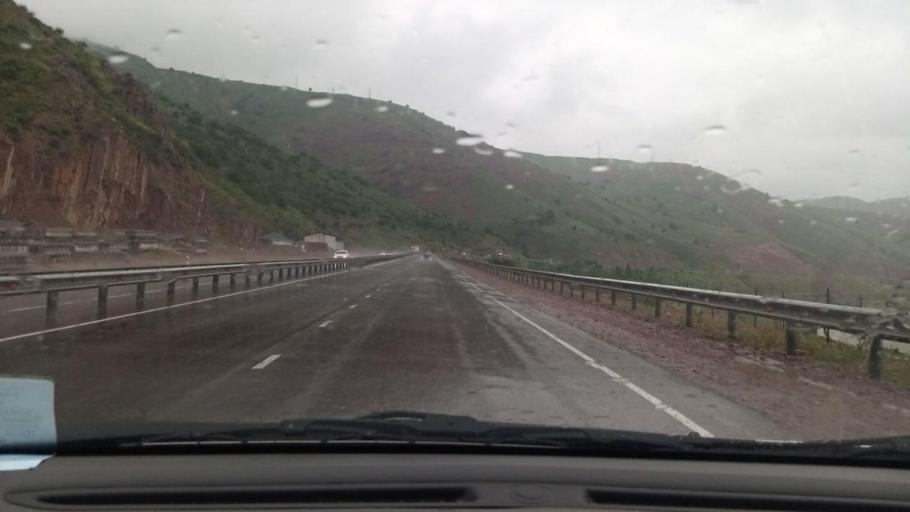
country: UZ
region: Toshkent
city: Angren
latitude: 41.0878
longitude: 70.3222
